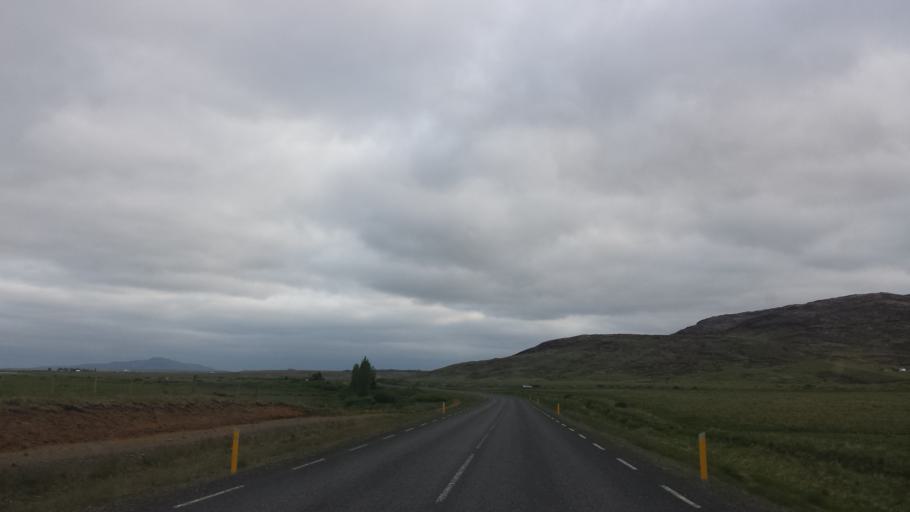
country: IS
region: South
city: Selfoss
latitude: 64.1404
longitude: -20.5692
